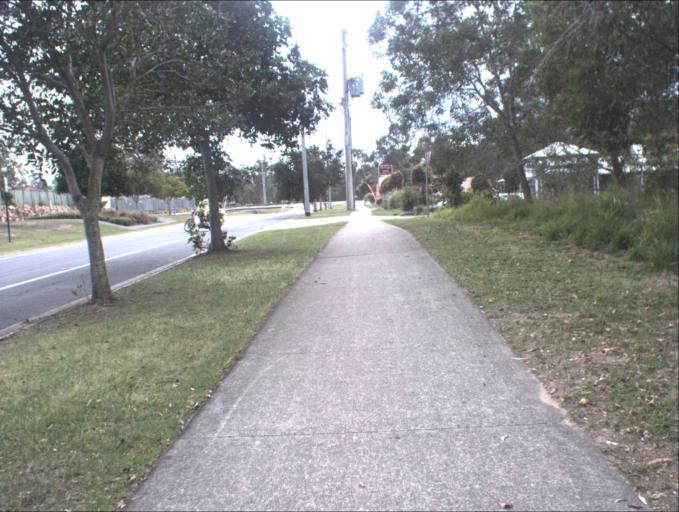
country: AU
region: Queensland
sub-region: Logan
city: Park Ridge South
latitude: -27.6888
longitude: 153.0572
